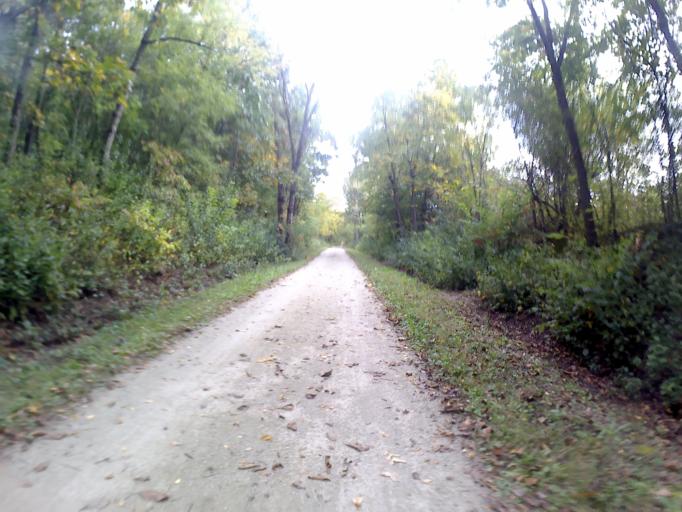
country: US
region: Illinois
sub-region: DuPage County
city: West Chicago
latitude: 41.9184
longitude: -88.2058
